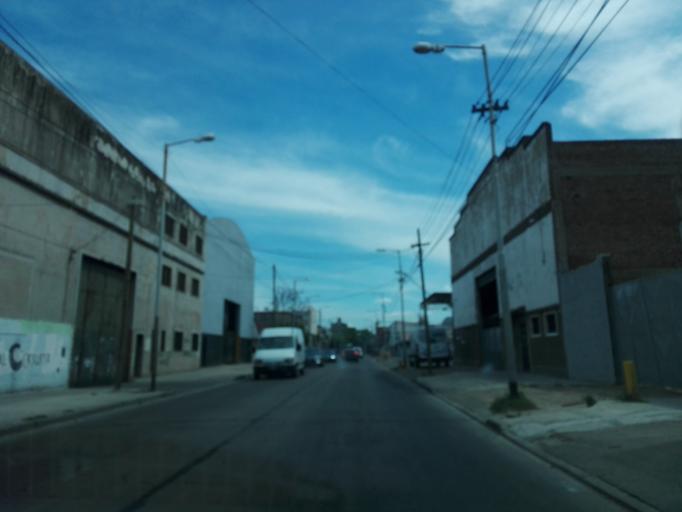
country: AR
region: Buenos Aires
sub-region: Partido de Avellaneda
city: Avellaneda
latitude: -34.6939
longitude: -58.3574
